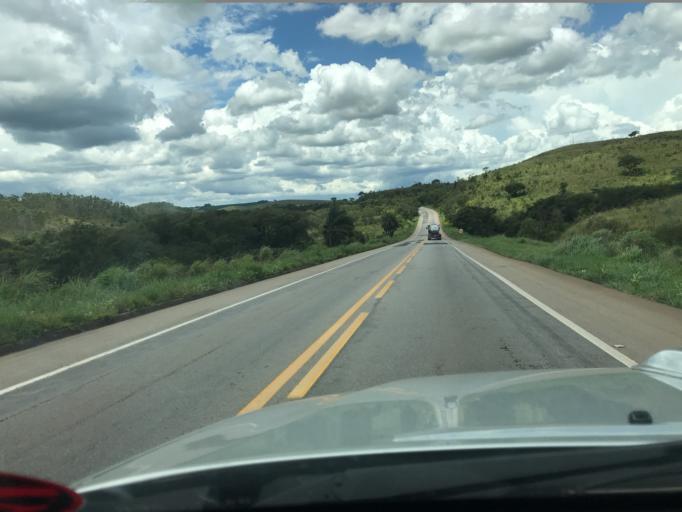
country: BR
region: Minas Gerais
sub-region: Ibia
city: Ibia
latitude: -19.5806
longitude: -46.4221
